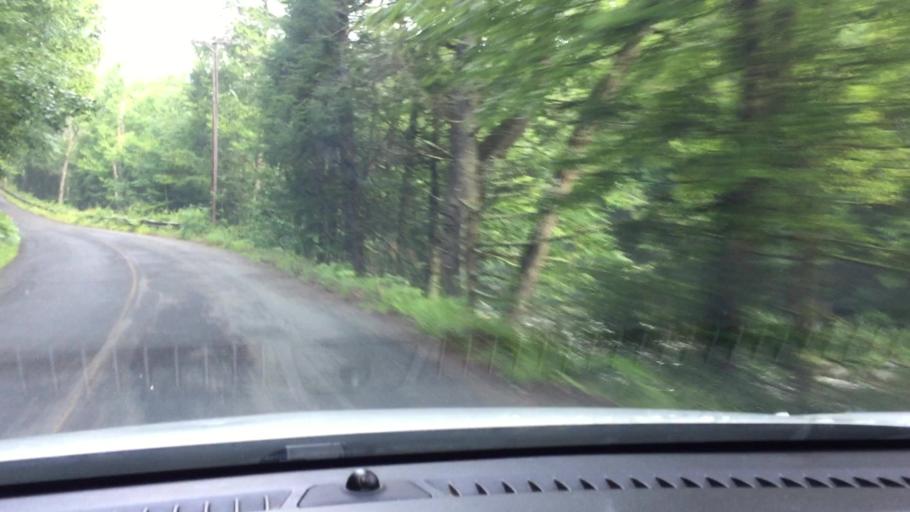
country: US
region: Massachusetts
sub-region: Hampshire County
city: Chesterfield
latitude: 42.3099
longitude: -72.9135
